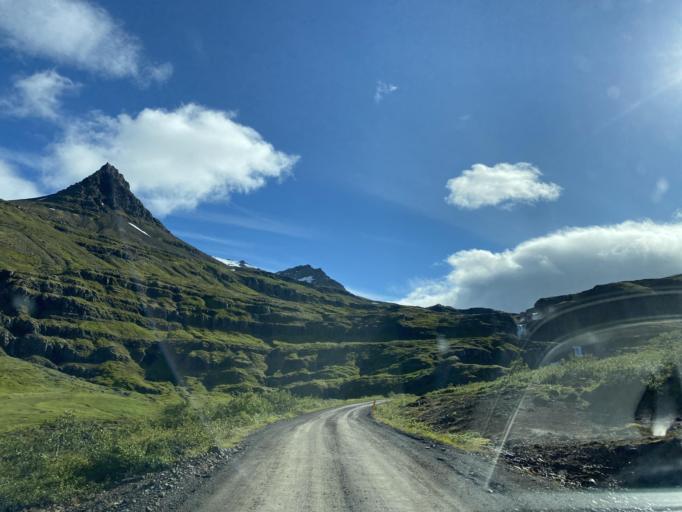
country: IS
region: East
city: Eskifjoerdur
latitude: 65.1813
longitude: -14.0758
